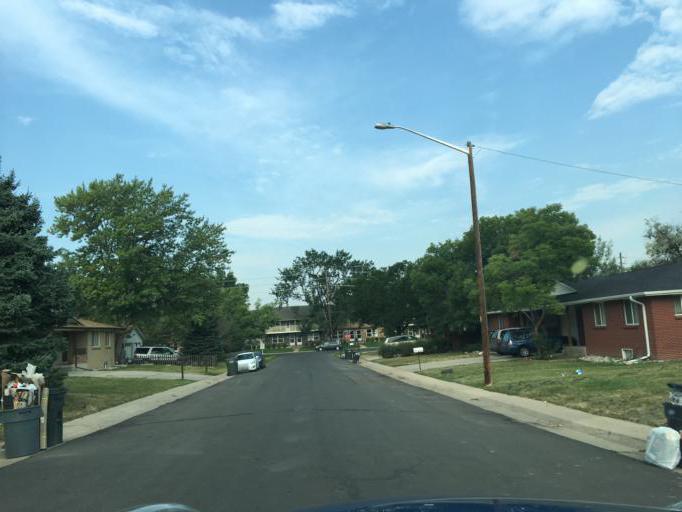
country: US
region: Colorado
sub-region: Jefferson County
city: Wheat Ridge
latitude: 39.7539
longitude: -105.1055
